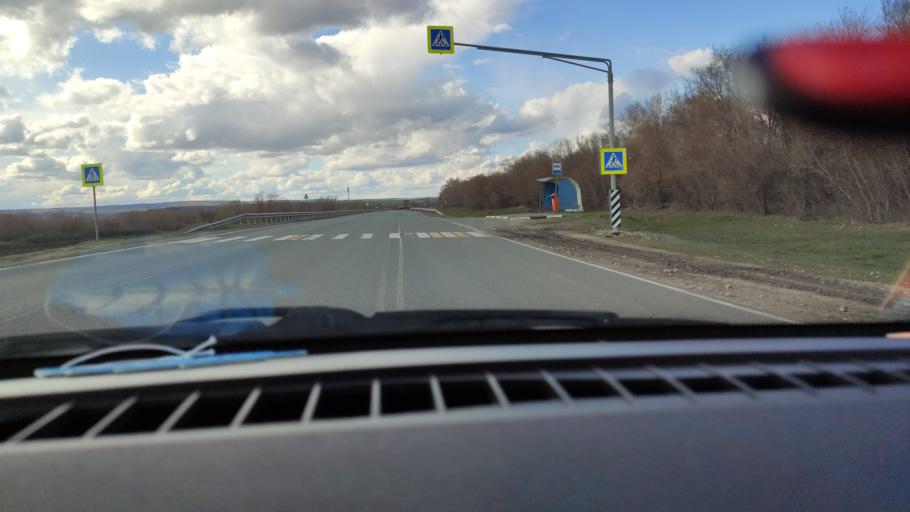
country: RU
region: Saratov
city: Tersa
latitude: 52.0881
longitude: 47.5484
